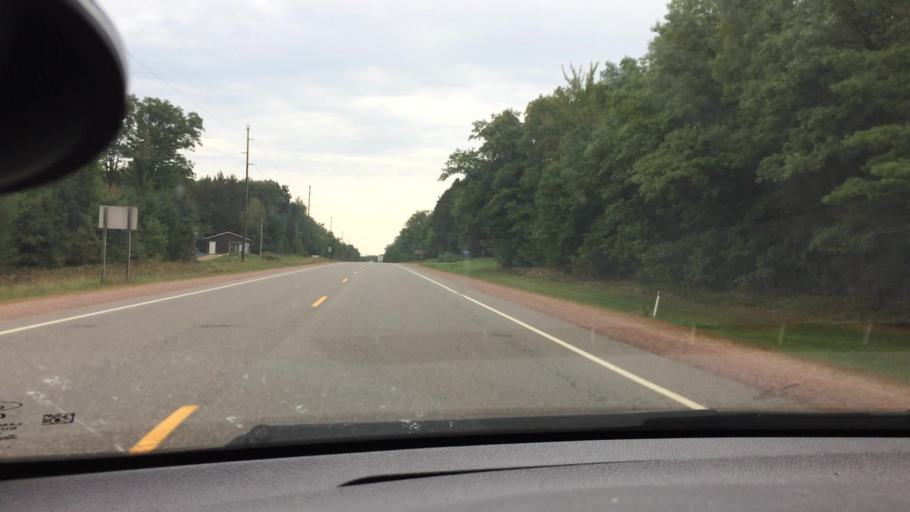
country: US
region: Wisconsin
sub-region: Clark County
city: Neillsville
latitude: 44.5737
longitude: -90.7315
